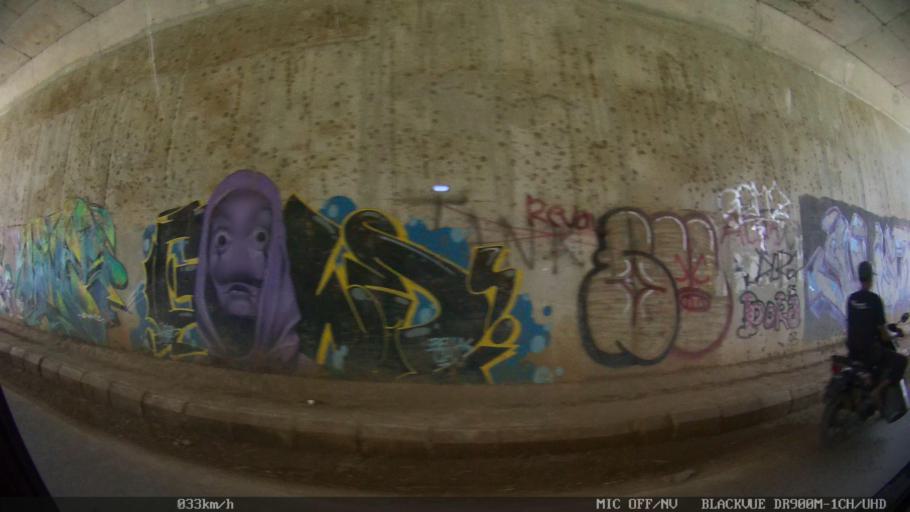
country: ID
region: Lampung
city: Kedaton
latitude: -5.3274
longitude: 105.2834
